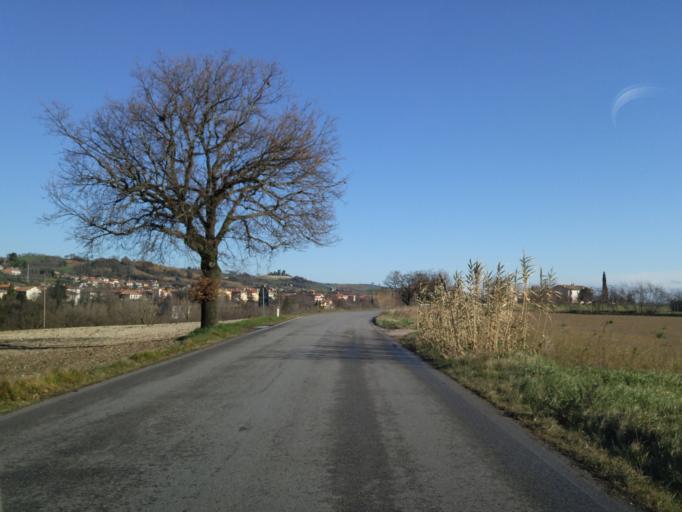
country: IT
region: The Marches
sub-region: Provincia di Pesaro e Urbino
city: Fossombrone
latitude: 43.6864
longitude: 12.8173
